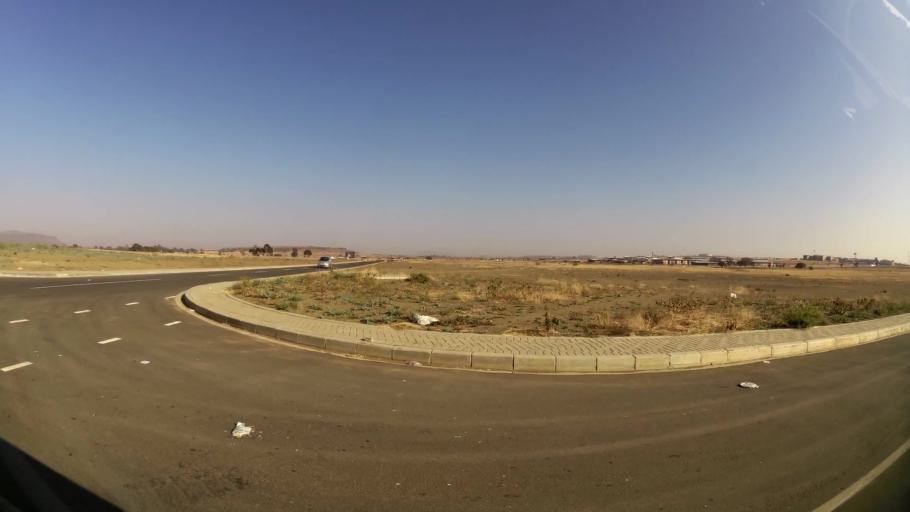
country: ZA
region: Orange Free State
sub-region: Mangaung Metropolitan Municipality
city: Bloemfontein
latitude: -29.1929
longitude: 26.2184
